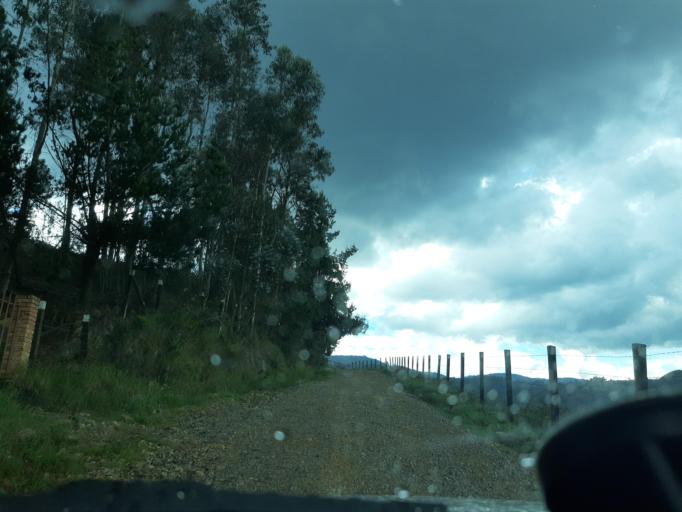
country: CO
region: Boyaca
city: Raquira
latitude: 5.4927
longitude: -73.7014
